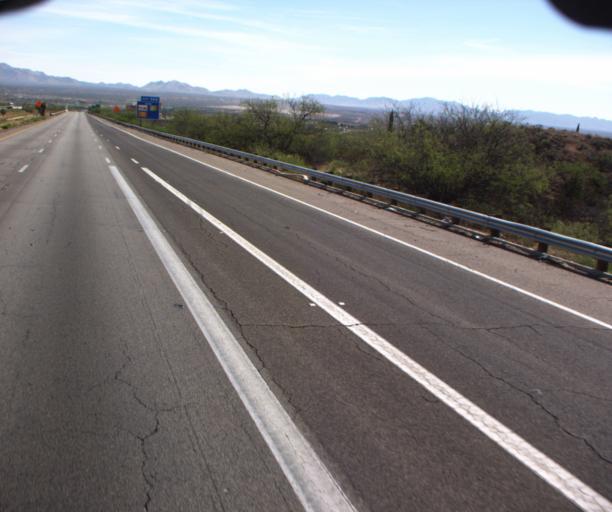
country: US
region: Arizona
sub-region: Cochise County
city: Benson
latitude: 31.9746
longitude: -110.3200
